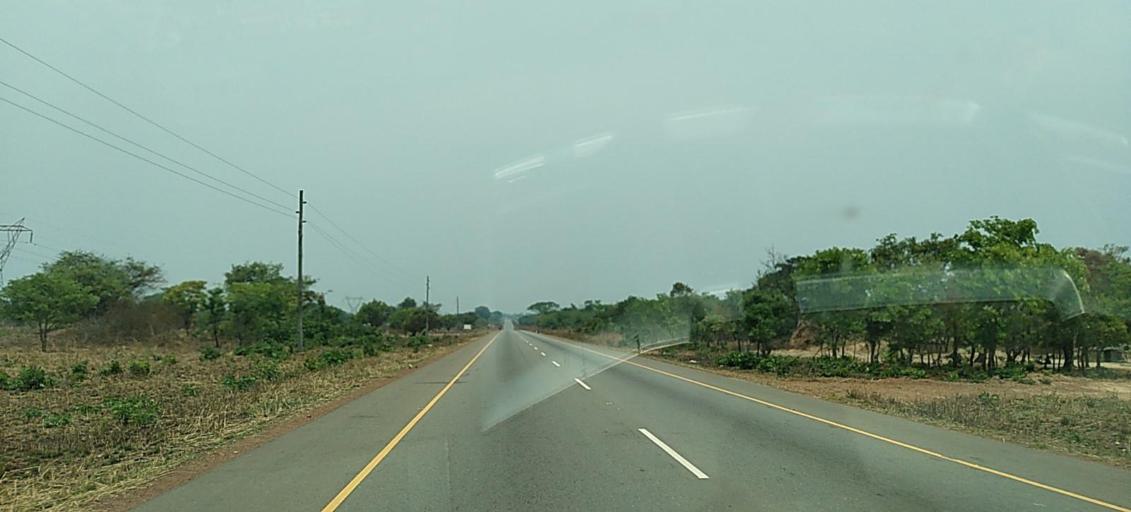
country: ZM
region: Copperbelt
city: Chililabombwe
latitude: -12.5032
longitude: 27.5429
